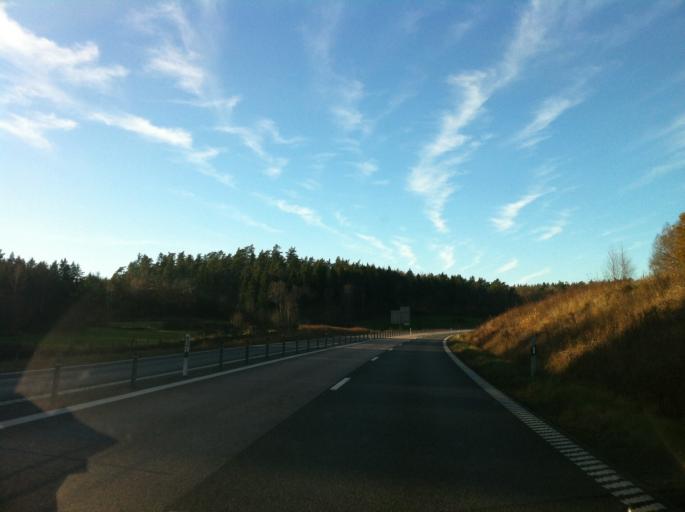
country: SE
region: Blekinge
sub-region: Karlshamns Kommun
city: Karlshamn
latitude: 56.1872
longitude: 14.9094
